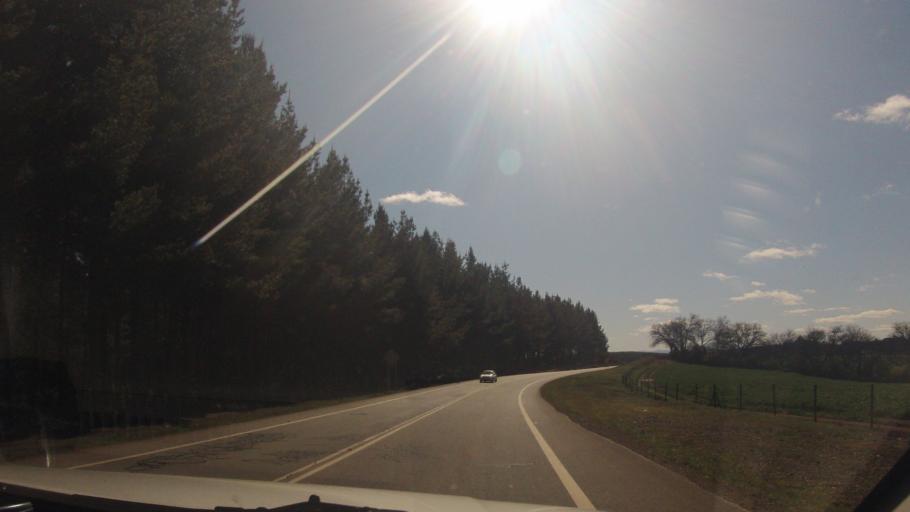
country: CL
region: Araucania
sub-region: Provincia de Malleco
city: Traiguen
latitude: -38.1991
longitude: -72.8016
